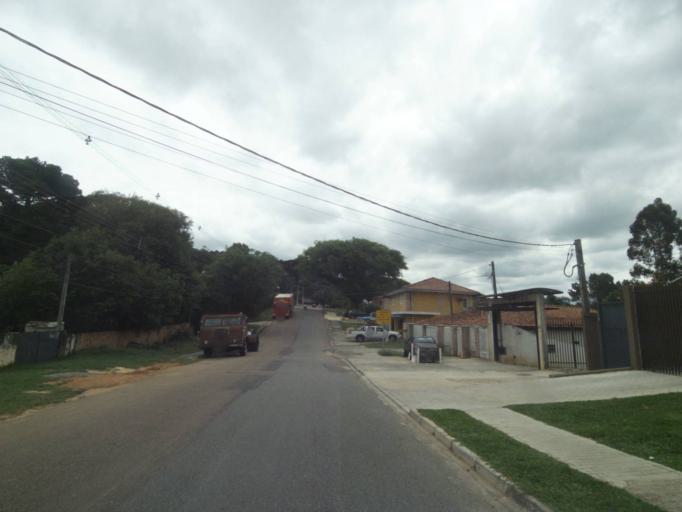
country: BR
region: Parana
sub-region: Curitiba
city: Curitiba
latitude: -25.3884
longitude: -49.2874
